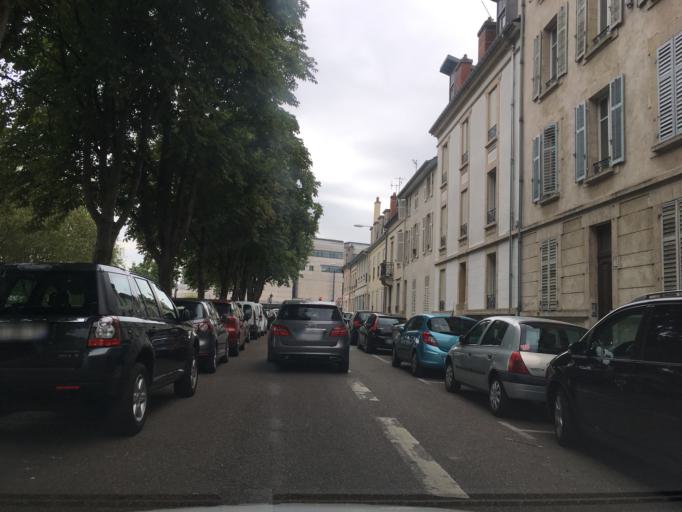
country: FR
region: Lorraine
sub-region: Departement de Meurthe-et-Moselle
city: Saint-Max
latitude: 48.6970
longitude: 6.1958
